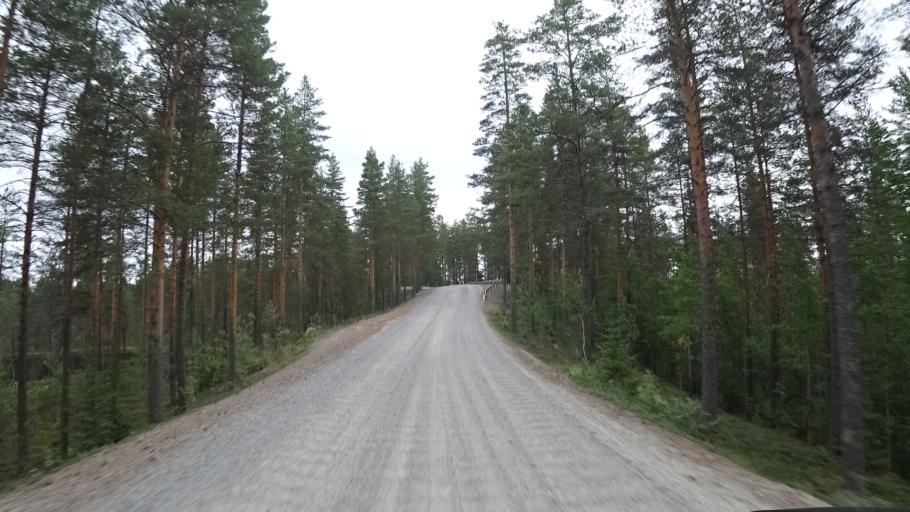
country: FI
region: North Karelia
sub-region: Pielisen Karjala
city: Lieksa
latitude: 63.2609
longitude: 30.3213
